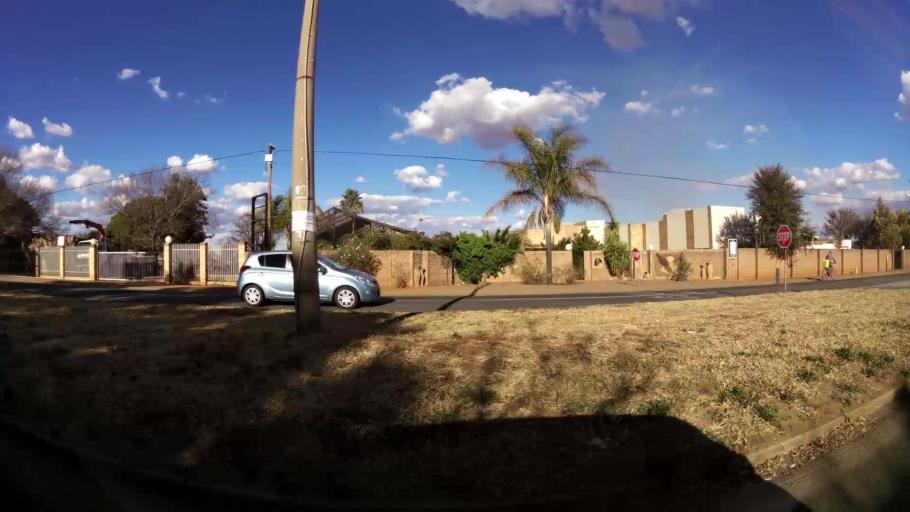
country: ZA
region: North-West
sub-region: Dr Kenneth Kaunda District Municipality
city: Klerksdorp
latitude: -26.8386
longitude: 26.6588
